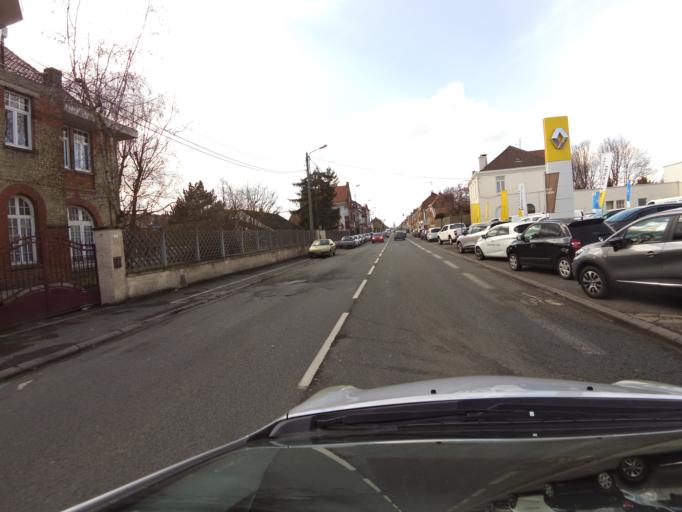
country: FR
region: Nord-Pas-de-Calais
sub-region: Departement du Nord
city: Armentieres
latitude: 50.6959
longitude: 2.8610
